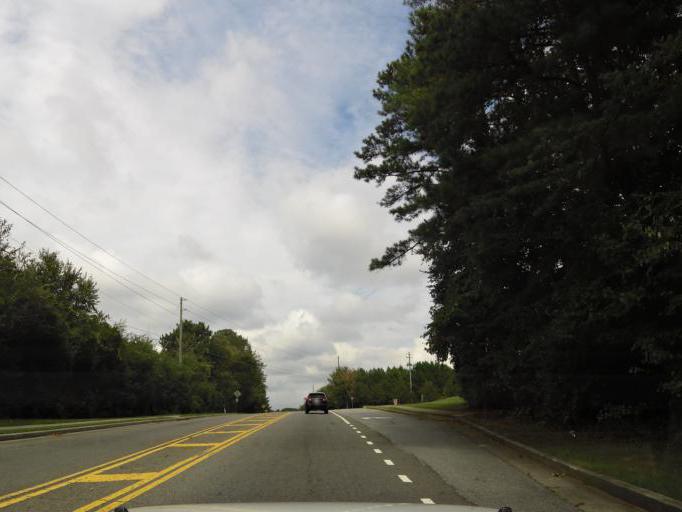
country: US
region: Georgia
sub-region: Cobb County
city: Kennesaw
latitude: 33.9978
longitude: -84.6276
